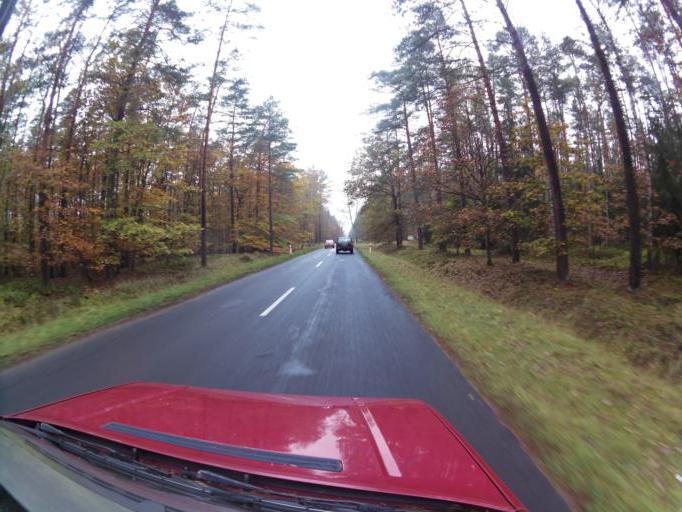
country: PL
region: West Pomeranian Voivodeship
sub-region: Powiat policki
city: Dobra
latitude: 53.5642
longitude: 14.4436
